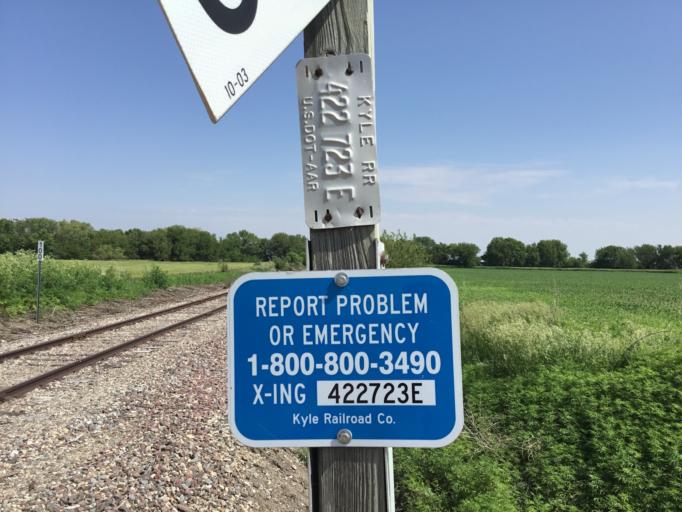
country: US
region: Kansas
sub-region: Republic County
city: Belleville
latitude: 39.7264
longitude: -97.7778
